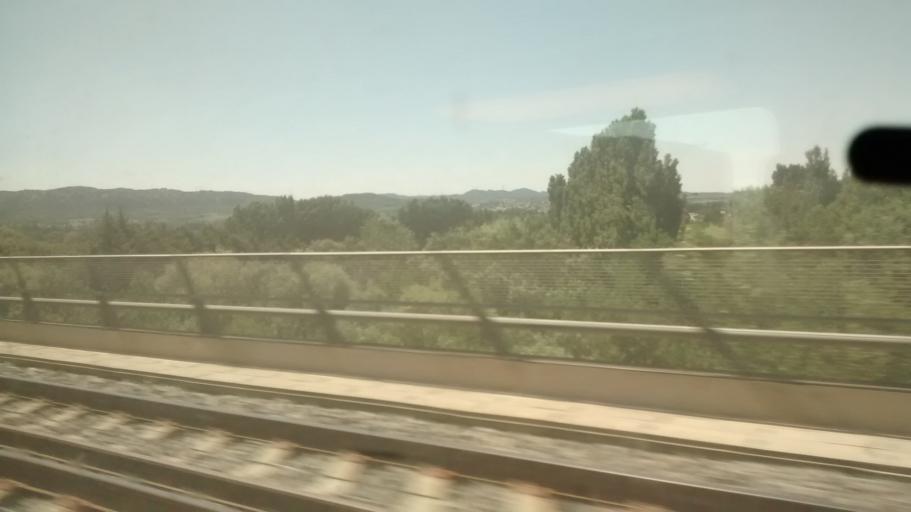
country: FR
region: Languedoc-Roussillon
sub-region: Departement du Gard
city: Montfaucon
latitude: 44.0704
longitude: 4.7643
